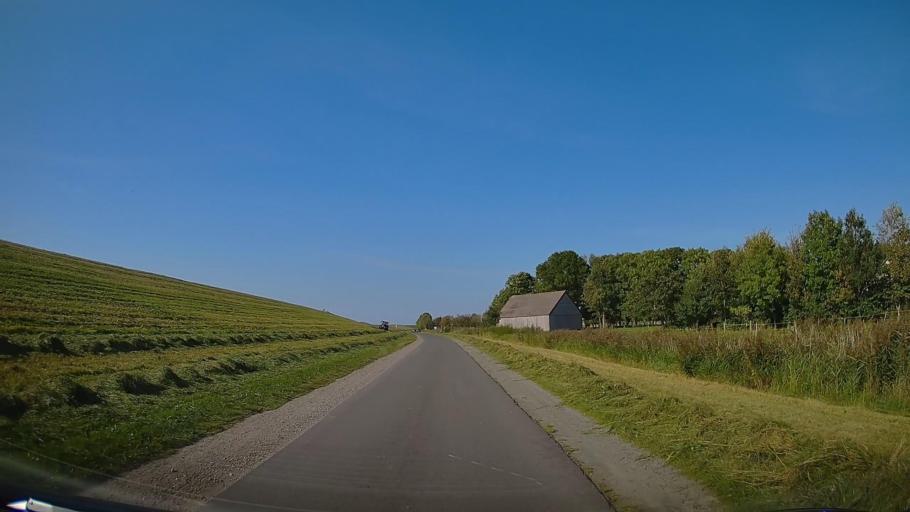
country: DE
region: Lower Saxony
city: Wremen
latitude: 53.6574
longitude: 8.4923
